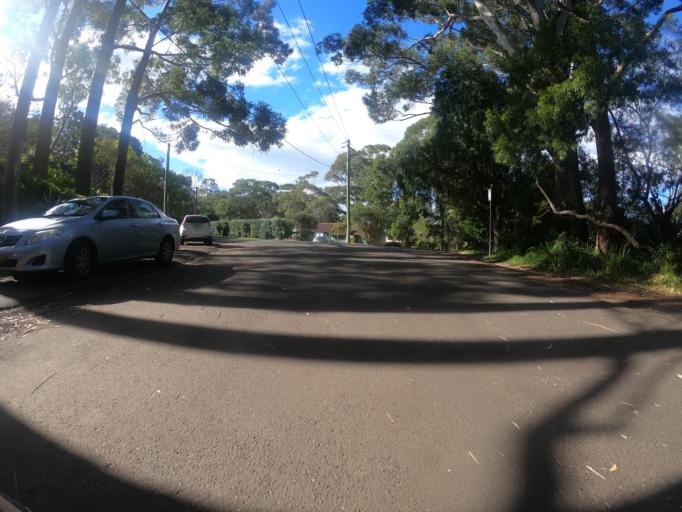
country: AU
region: New South Wales
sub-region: Wollongong
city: Bulli
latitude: -34.3024
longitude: 150.9271
